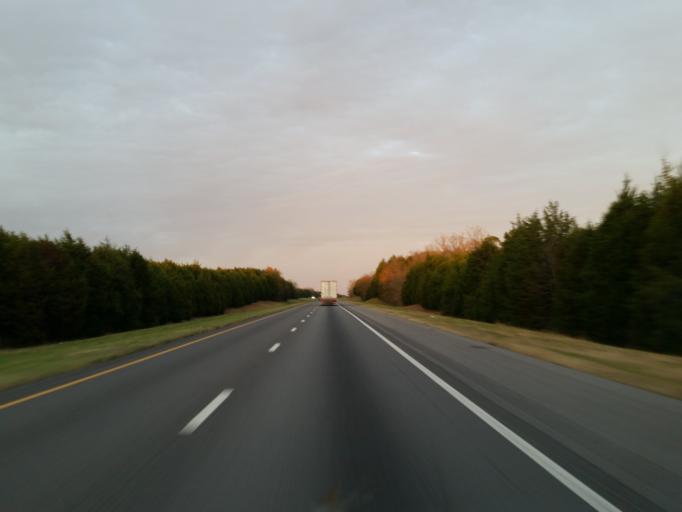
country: US
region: Alabama
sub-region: Sumter County
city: Livingston
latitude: 32.6466
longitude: -88.1943
